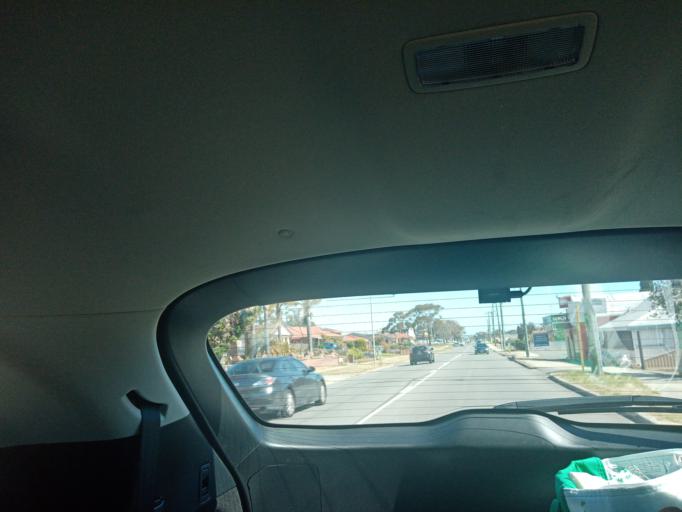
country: AU
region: Western Australia
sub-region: City of Cockburn
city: Spearwood
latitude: -32.1126
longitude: 115.7827
